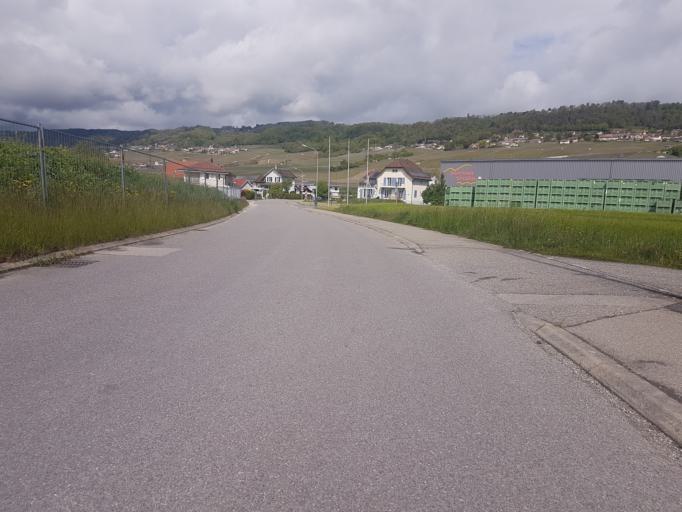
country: CH
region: Vaud
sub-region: Nyon District
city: Perroy
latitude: 46.4691
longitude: 6.3616
